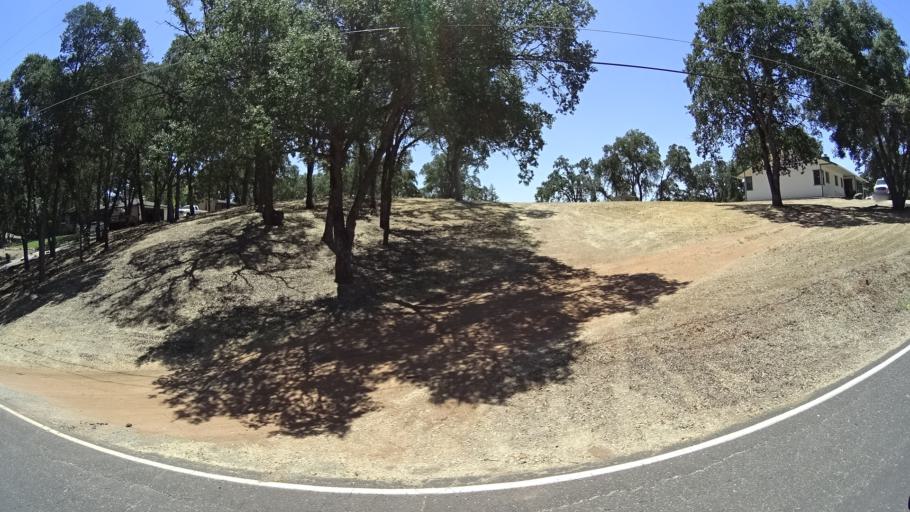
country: US
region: California
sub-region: Calaveras County
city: Rancho Calaveras
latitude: 38.1282
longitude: -120.8691
